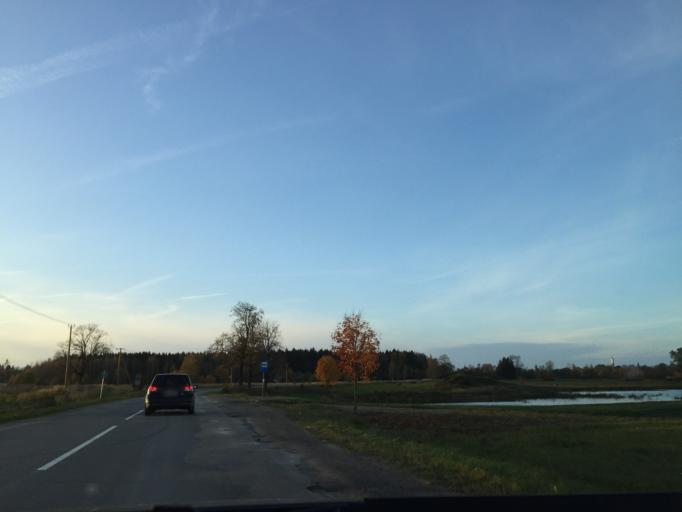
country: LV
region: Malpils
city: Malpils
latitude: 56.8936
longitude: 24.9319
